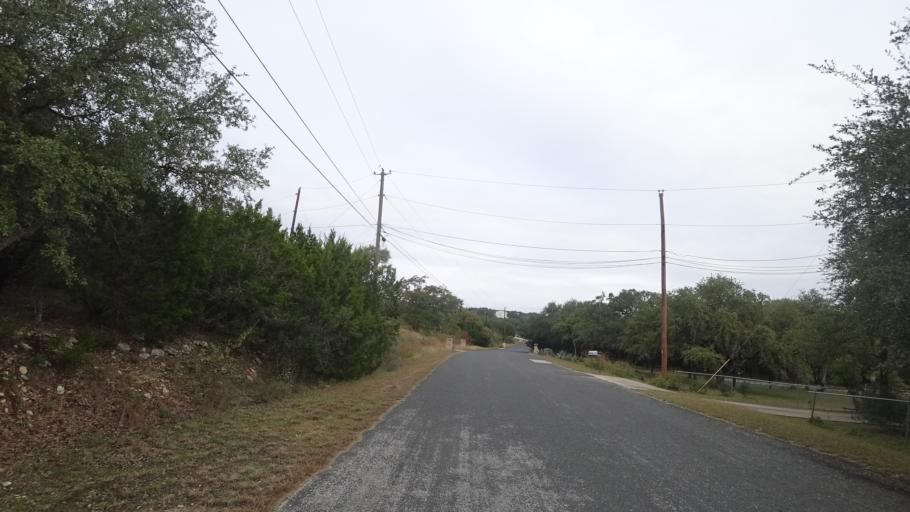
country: US
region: Texas
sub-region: Travis County
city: Hudson Bend
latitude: 30.3860
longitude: -97.9171
